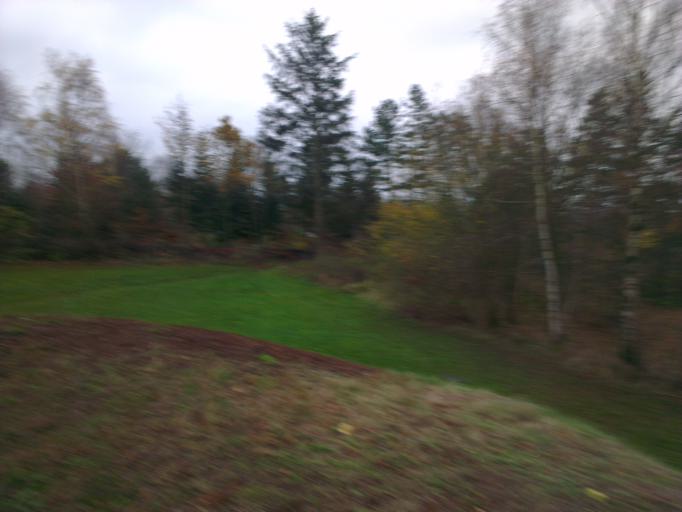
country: DK
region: Capital Region
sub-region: Frederikssund Kommune
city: Jaegerspris
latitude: 55.8506
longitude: 12.0038
